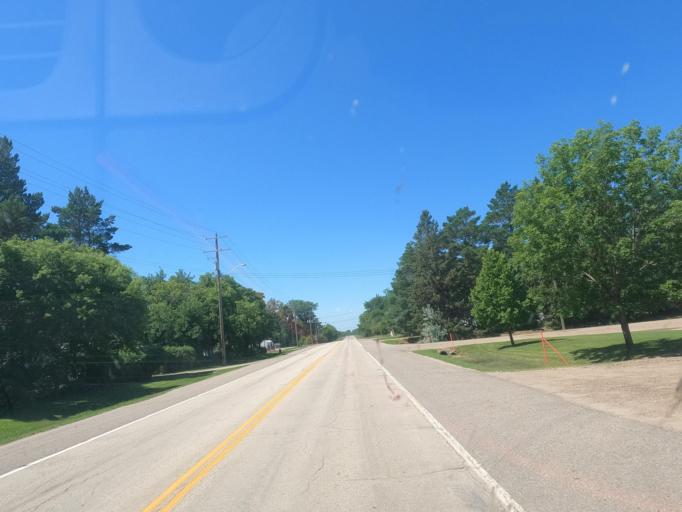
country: CA
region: Manitoba
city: Souris
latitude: 49.6211
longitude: -100.2708
